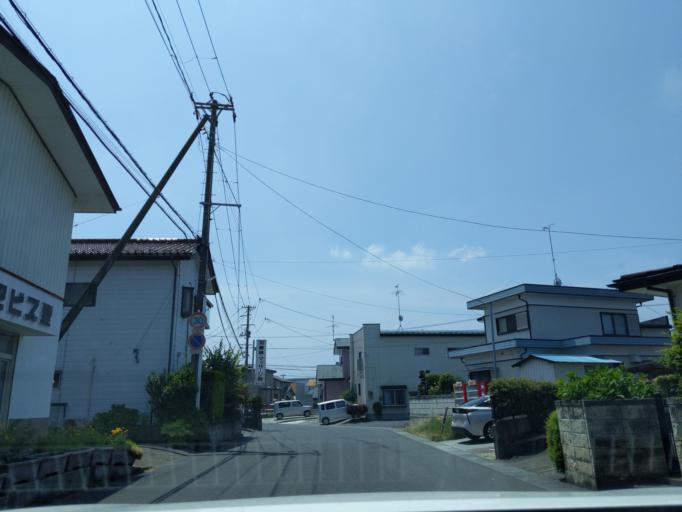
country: JP
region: Fukushima
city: Koriyama
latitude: 37.3707
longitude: 140.3571
